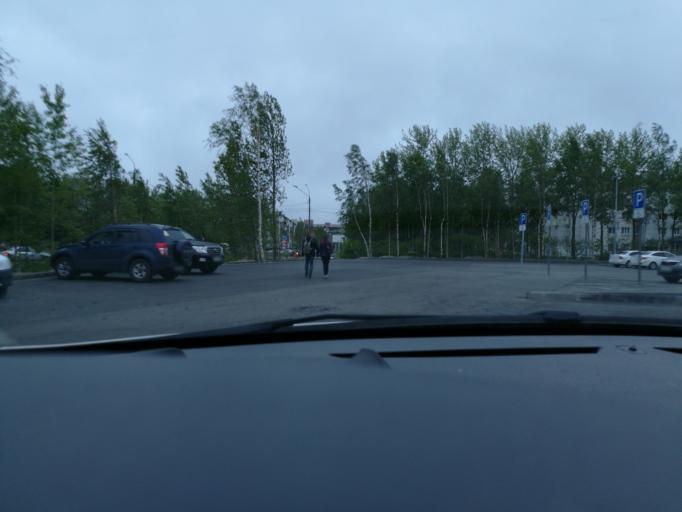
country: RU
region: Arkhangelskaya
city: Severodvinsk
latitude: 64.5567
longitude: 39.7763
